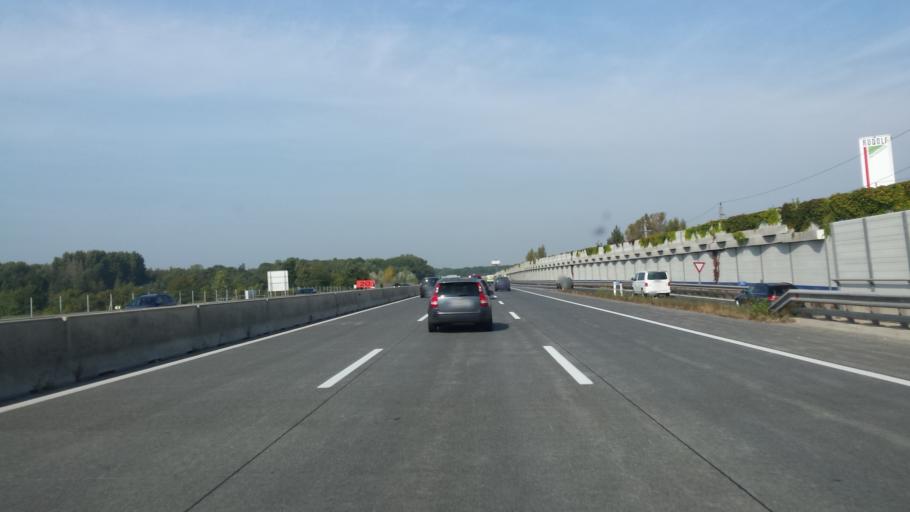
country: AT
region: Lower Austria
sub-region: Politischer Bezirk Korneuburg
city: Leobendorf
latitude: 48.3616
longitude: 16.3058
